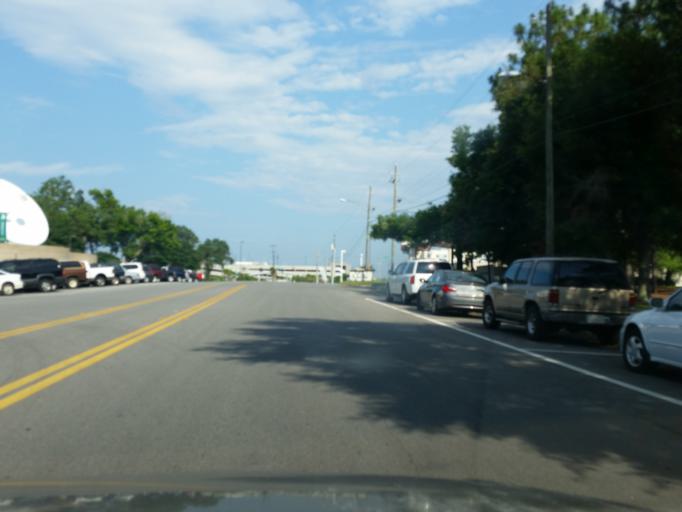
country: US
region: Florida
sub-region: Escambia County
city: Ferry Pass
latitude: 30.4783
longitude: -87.1995
